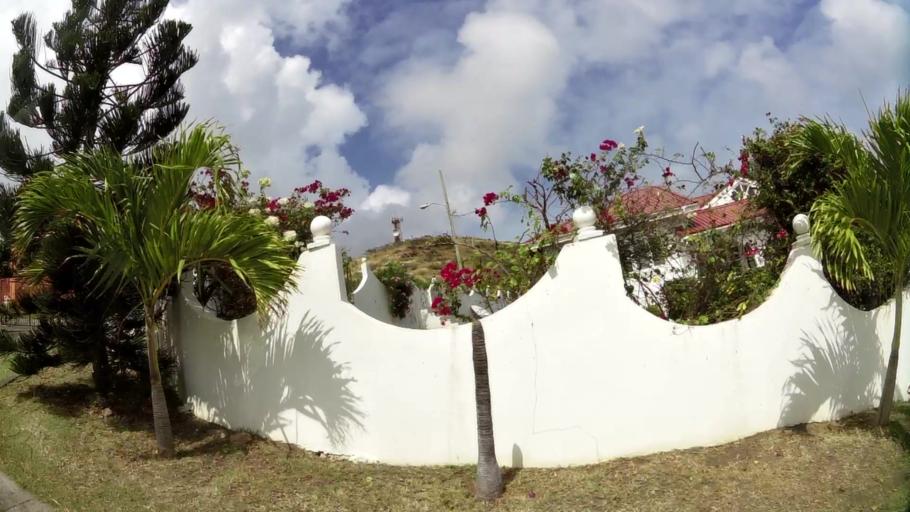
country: KN
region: Saint Peter Basseterre
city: Monkey Hill
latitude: 17.2958
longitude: -62.6940
